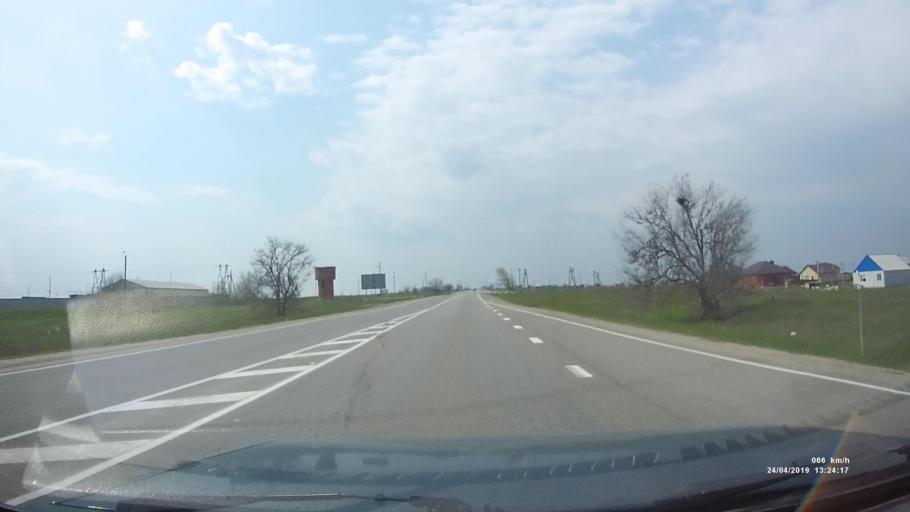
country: RU
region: Kalmykiya
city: Elista
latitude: 46.2844
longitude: 44.2574
